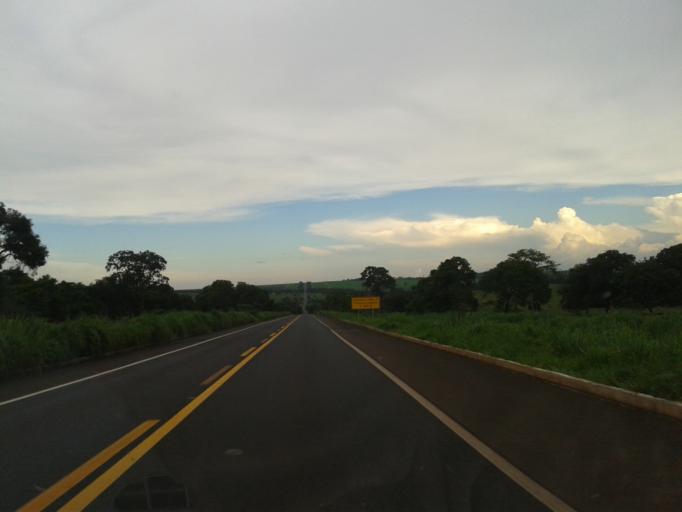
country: BR
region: Minas Gerais
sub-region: Santa Vitoria
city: Santa Vitoria
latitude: -18.9100
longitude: -50.2176
